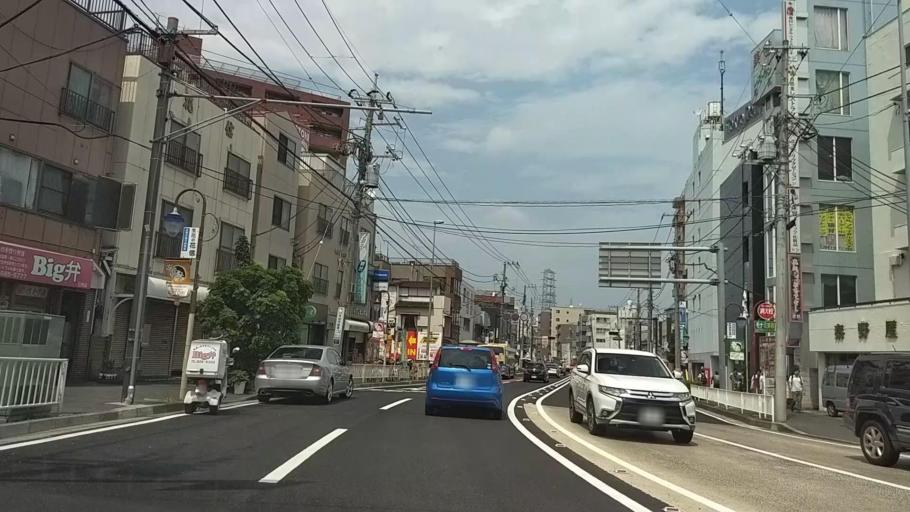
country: JP
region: Kanagawa
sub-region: Kawasaki-shi
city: Kawasaki
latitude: 35.5137
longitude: 139.6744
